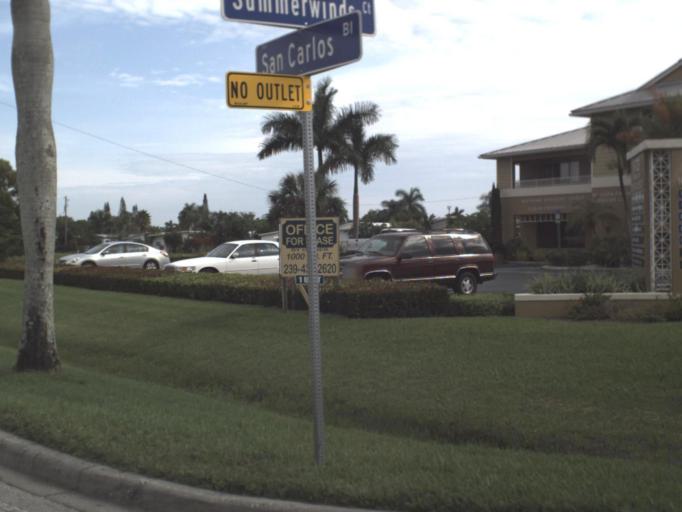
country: US
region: Florida
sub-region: Lee County
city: Harlem Heights
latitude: 26.5012
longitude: -81.9434
